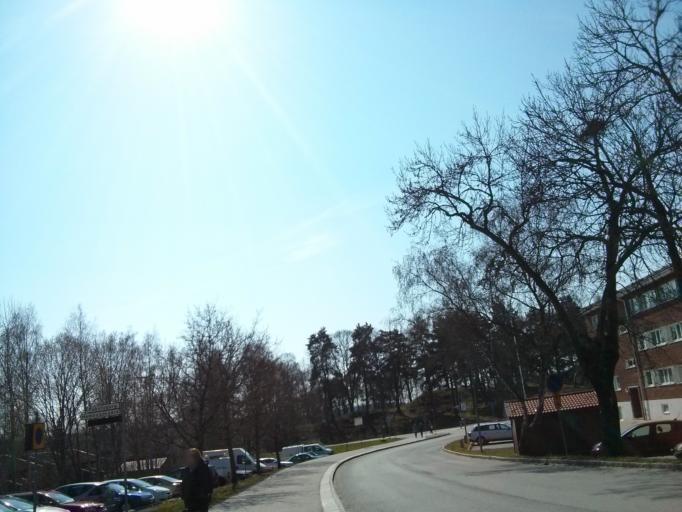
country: SE
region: Stockholm
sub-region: Upplands Vasby Kommun
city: Upplands Vaesby
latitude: 59.5183
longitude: 17.8942
